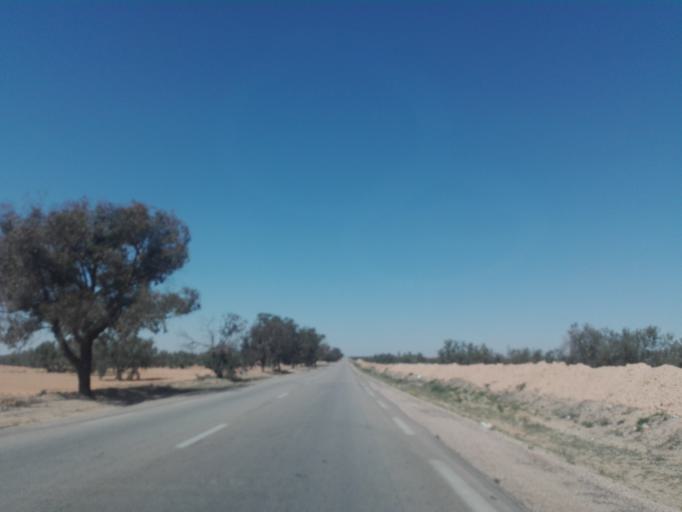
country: TN
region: Safaqis
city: Bi'r `Ali Bin Khalifah
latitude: 34.7570
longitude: 10.3231
